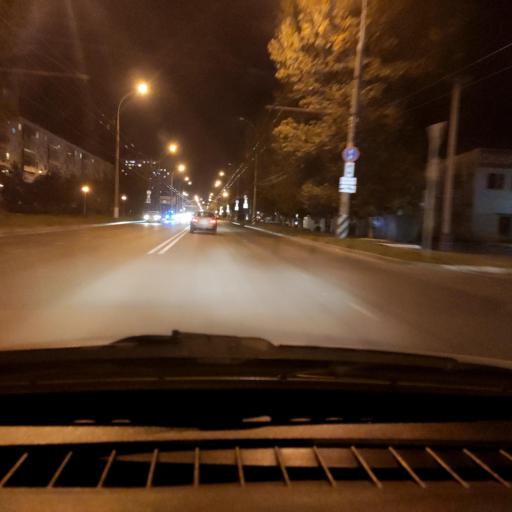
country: RU
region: Samara
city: Tol'yatti
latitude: 53.5358
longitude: 49.3031
